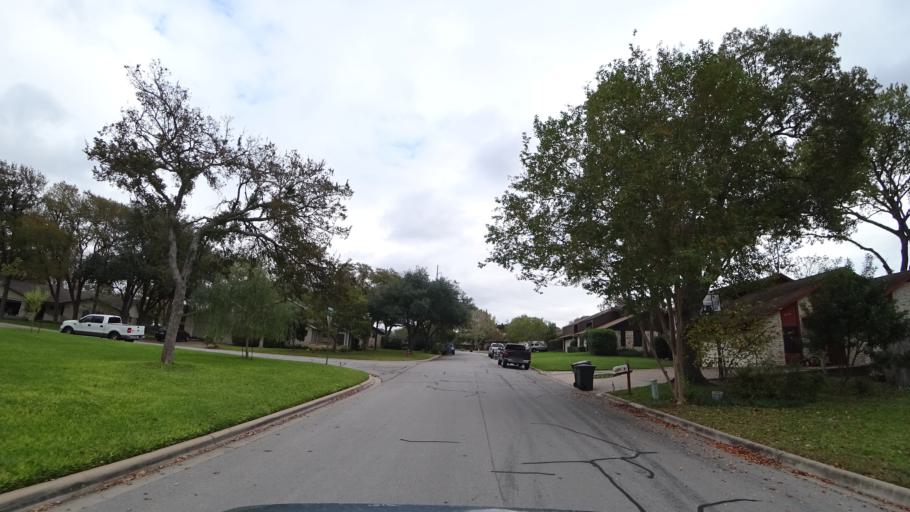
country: US
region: Texas
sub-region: Williamson County
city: Round Rock
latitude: 30.5009
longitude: -97.7002
